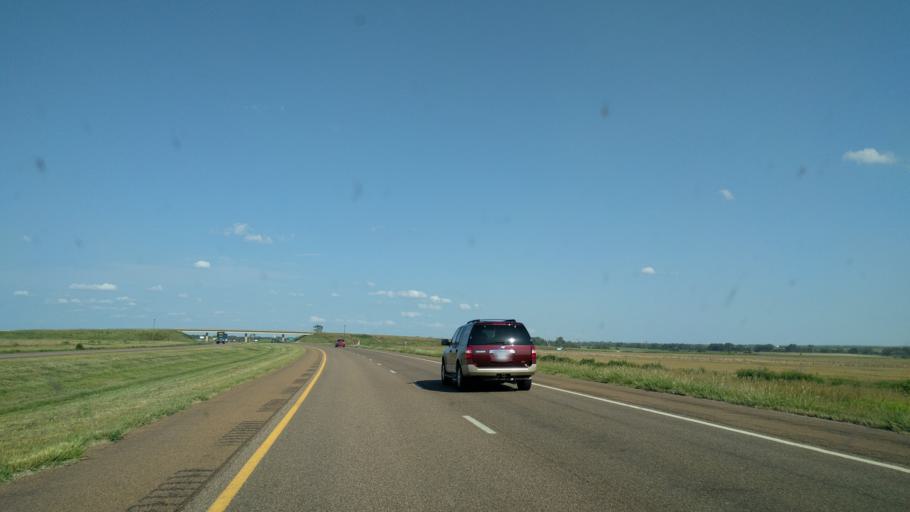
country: US
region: Kansas
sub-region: Ellis County
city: Ellis
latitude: 38.9513
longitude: -99.5994
